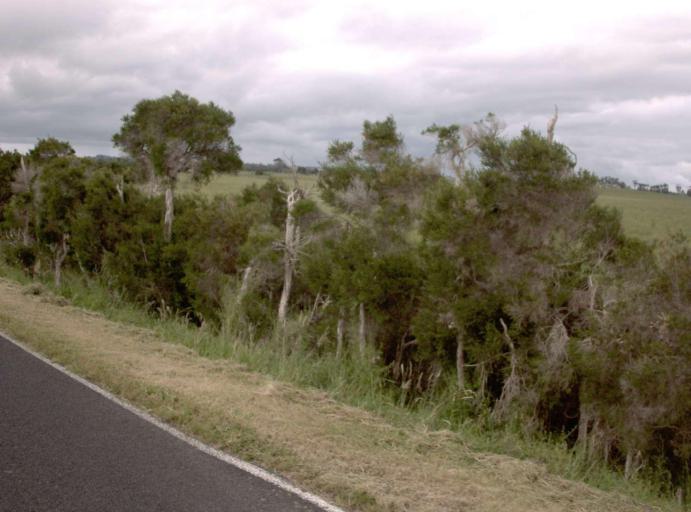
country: AU
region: Victoria
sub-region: Bass Coast
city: North Wonthaggi
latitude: -38.5649
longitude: 145.6331
